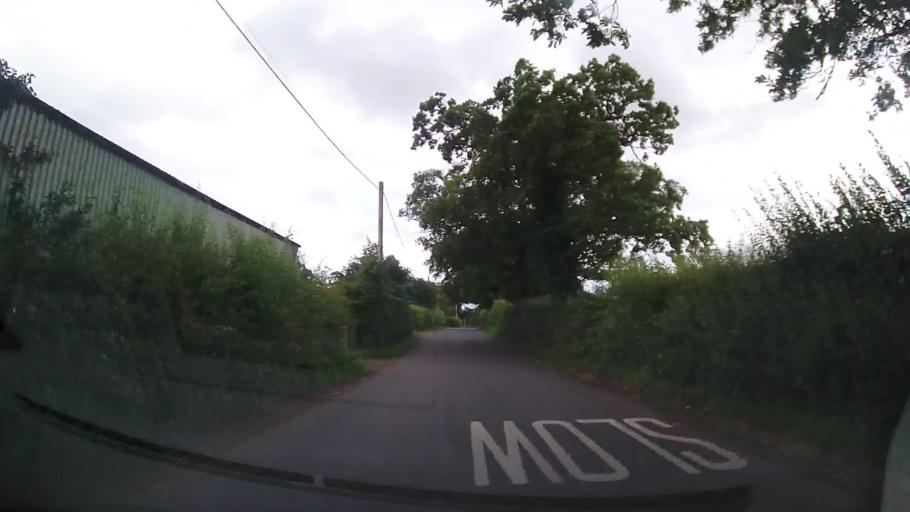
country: GB
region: England
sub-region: Shropshire
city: Wem
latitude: 52.8731
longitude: -2.7241
